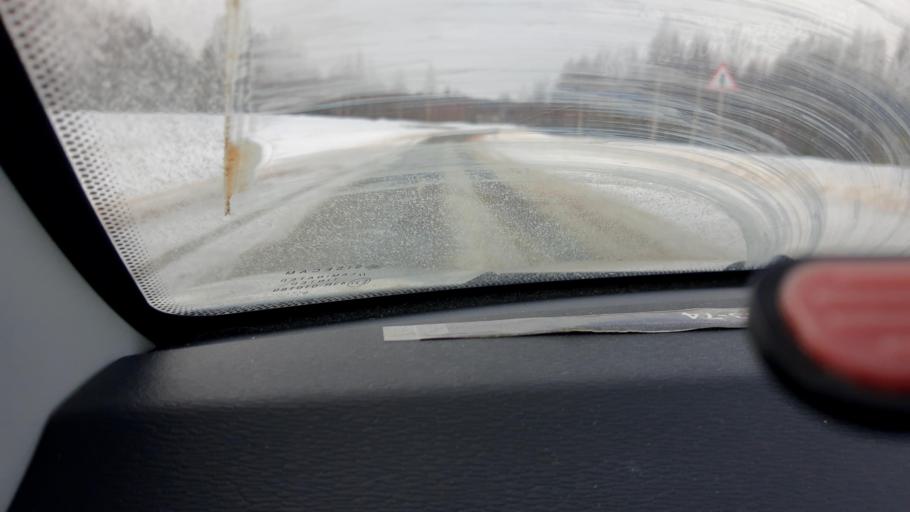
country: RU
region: Nizjnij Novgorod
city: Tonkino
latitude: 57.3488
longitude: 46.4411
